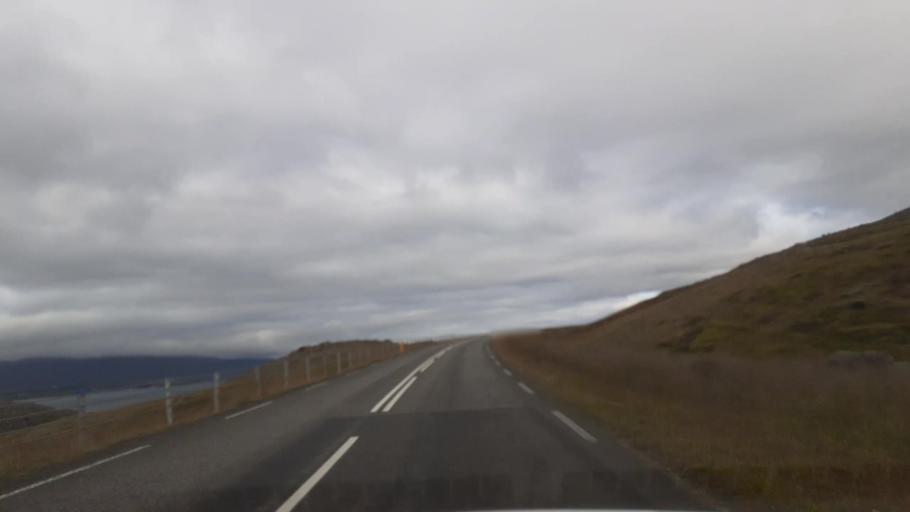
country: IS
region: Northeast
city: Akureyri
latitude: 65.8234
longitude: -18.0532
